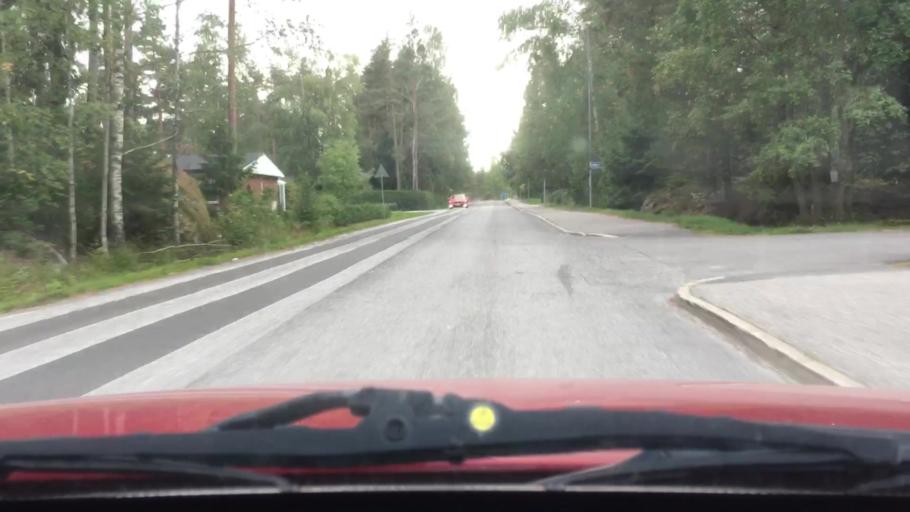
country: FI
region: Varsinais-Suomi
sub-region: Turku
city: Masku
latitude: 60.5507
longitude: 22.1339
